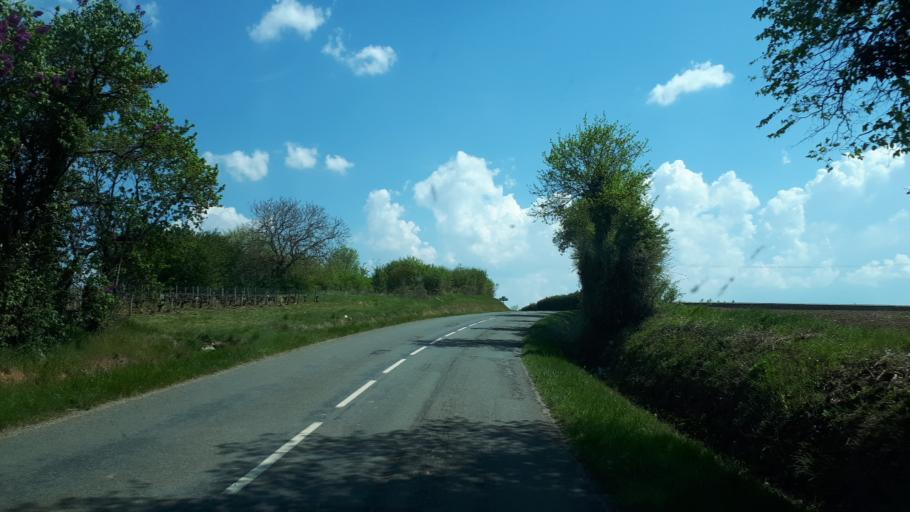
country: FR
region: Centre
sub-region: Departement du Cher
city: Sancerre
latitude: 47.3039
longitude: 2.7367
